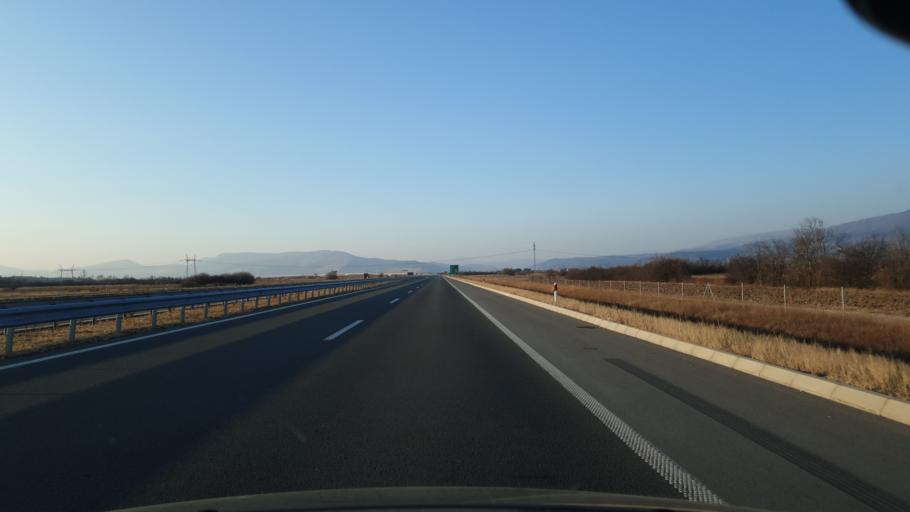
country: RS
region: Central Serbia
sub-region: Pirotski Okrug
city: Pirot
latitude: 43.1093
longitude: 22.6340
